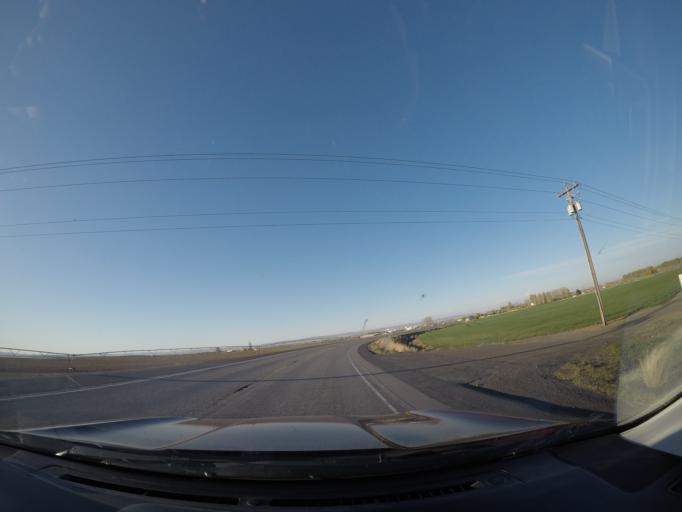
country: US
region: Washington
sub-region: Grant County
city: Quincy
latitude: 47.0886
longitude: -119.8634
